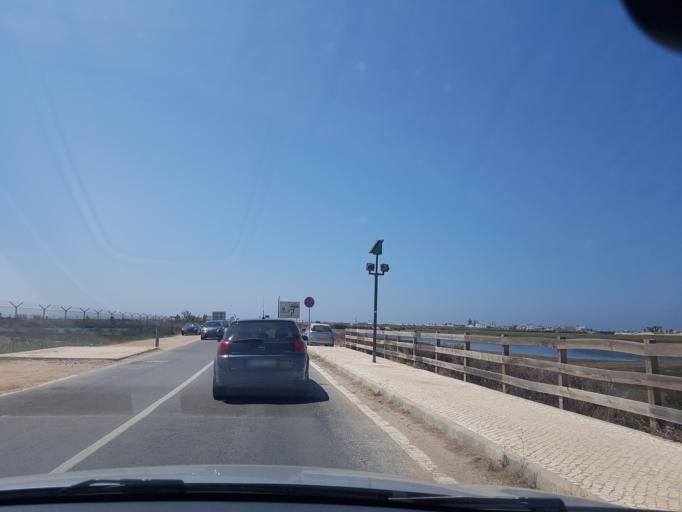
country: PT
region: Faro
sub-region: Faro
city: Faro
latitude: 37.0167
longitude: -7.9884
